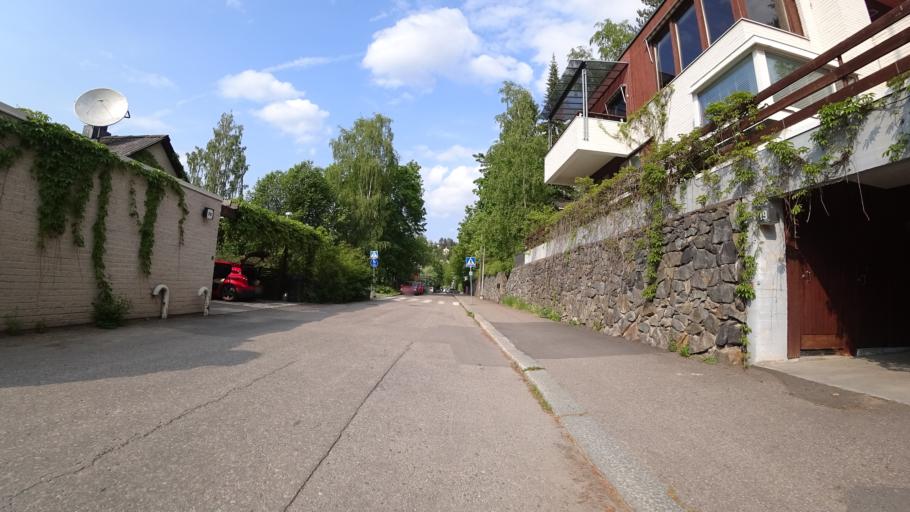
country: FI
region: Pirkanmaa
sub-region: Tampere
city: Tampere
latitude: 61.4966
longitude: 23.7125
